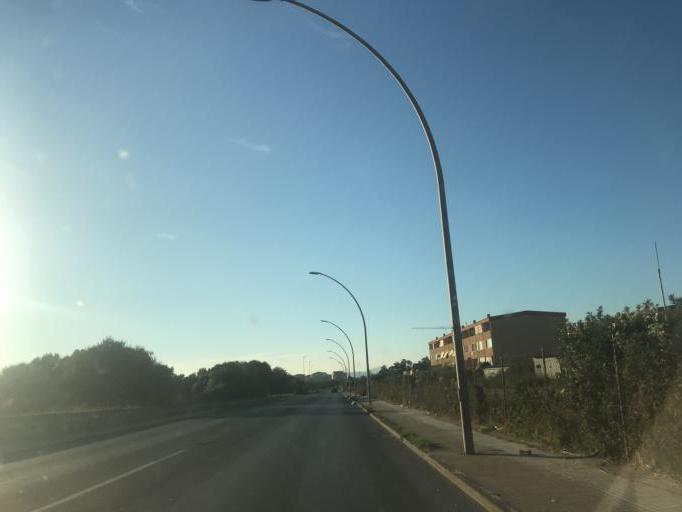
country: IT
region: Sardinia
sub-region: Provincia di Sassari
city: Alghero
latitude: 40.5661
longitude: 8.3307
